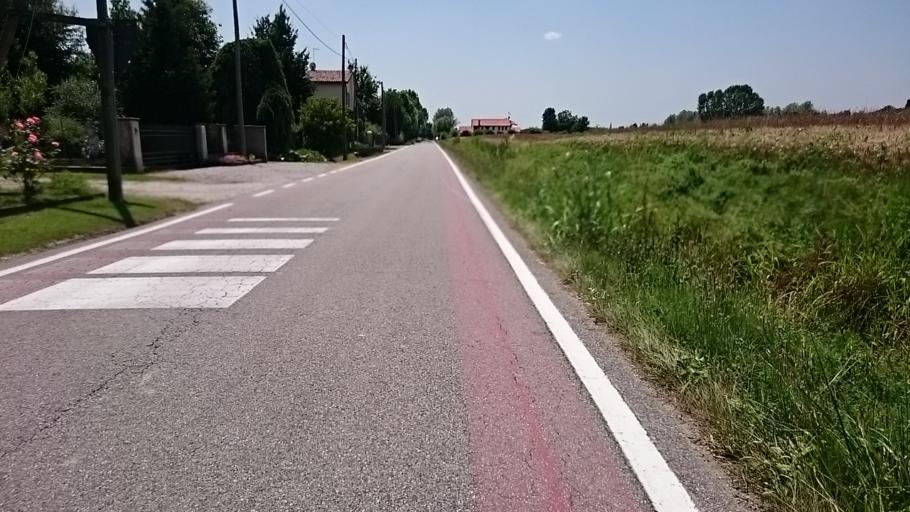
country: IT
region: Veneto
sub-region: Provincia di Padova
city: Villanova
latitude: 45.5063
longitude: 11.9836
